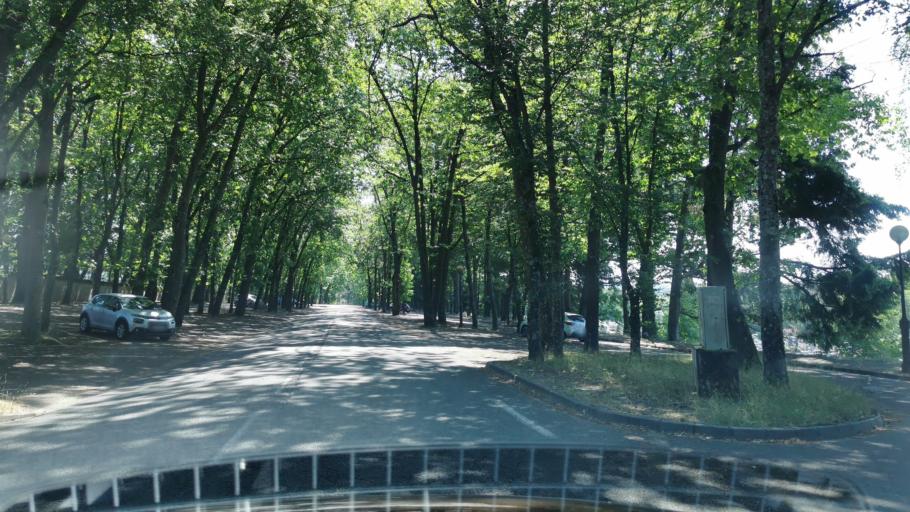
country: FR
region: Bourgogne
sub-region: Departement de Saone-et-Loire
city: Le Creusot
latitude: 46.8001
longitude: 4.4239
